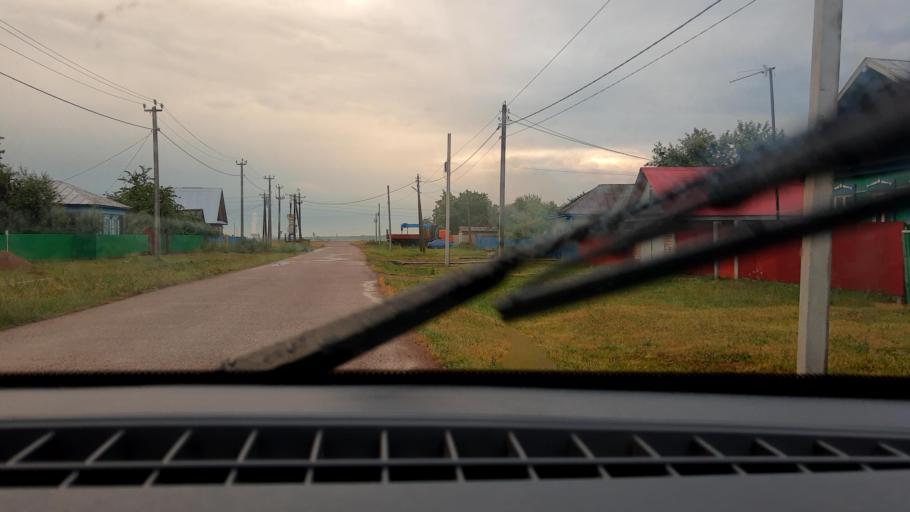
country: RU
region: Bashkortostan
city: Mikhaylovka
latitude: 54.8414
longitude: 55.8349
